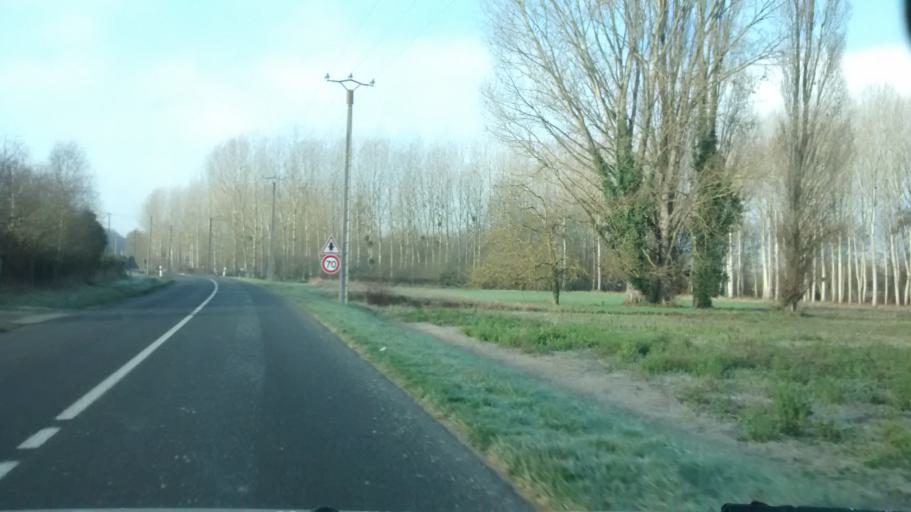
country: FR
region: Centre
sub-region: Departement d'Indre-et-Loire
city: Savonnieres
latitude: 47.3524
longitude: 0.5688
